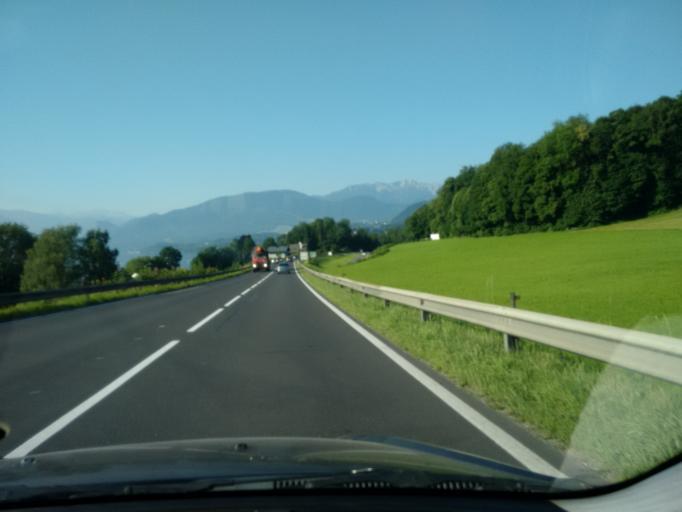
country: AT
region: Upper Austria
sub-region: Politischer Bezirk Gmunden
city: Altmunster
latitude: 47.9074
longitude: 13.7800
